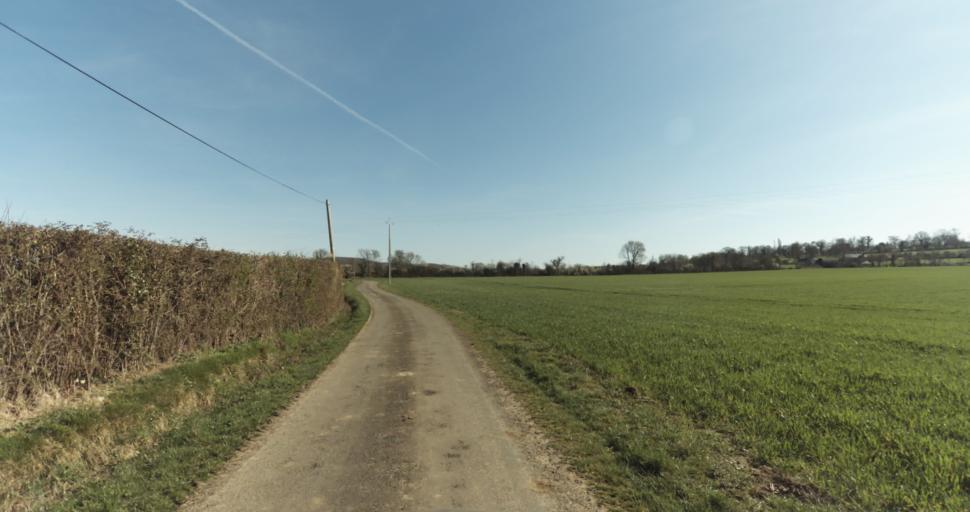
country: FR
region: Lower Normandy
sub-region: Departement du Calvados
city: Saint-Pierre-sur-Dives
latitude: 49.0345
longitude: 0.0071
